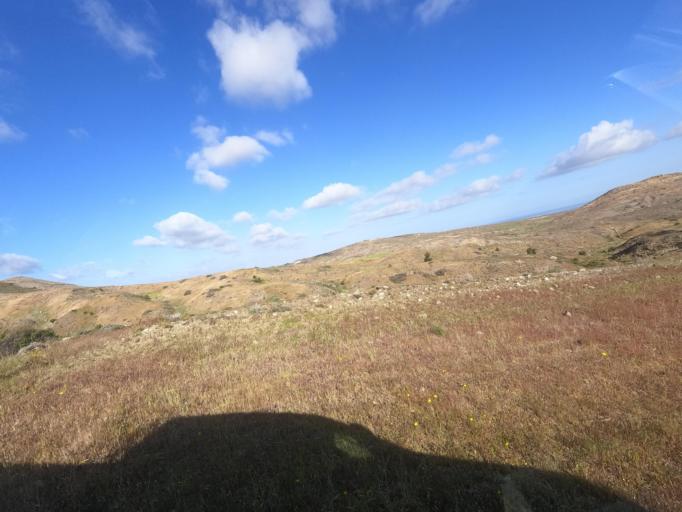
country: CY
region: Lefkosia
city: Astromeritis
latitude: 35.0748
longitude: 33.0398
